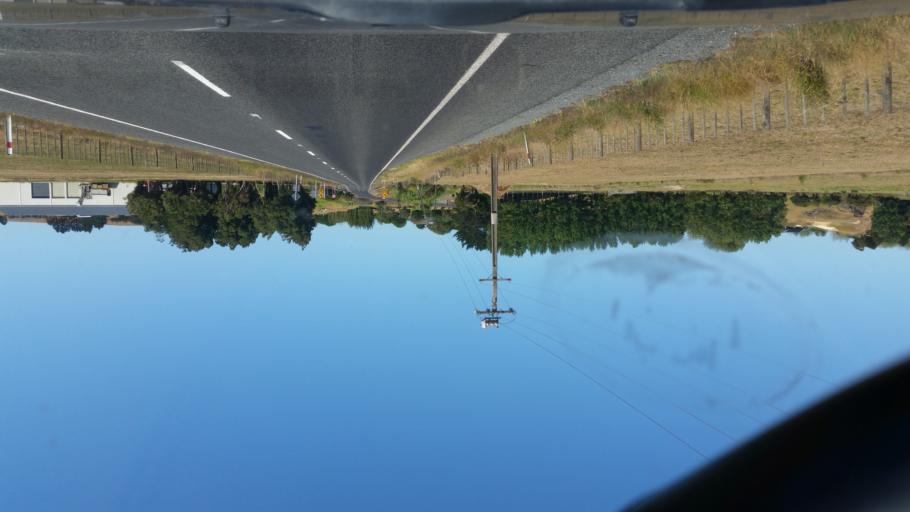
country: NZ
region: Northland
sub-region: Kaipara District
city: Dargaville
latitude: -35.9456
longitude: 173.8429
